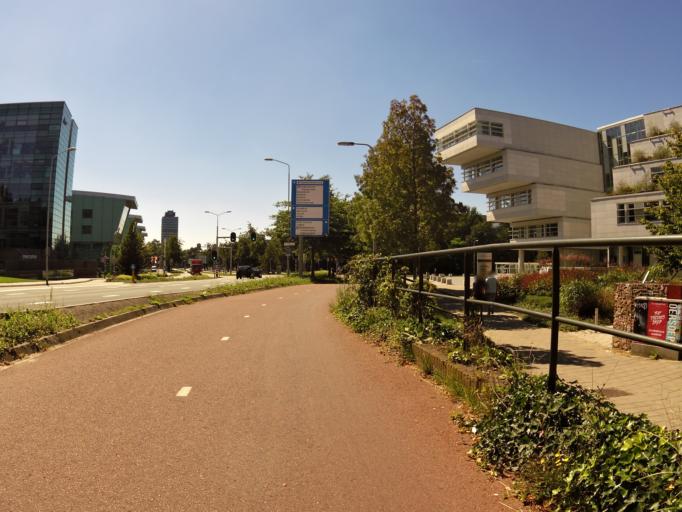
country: NL
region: Gelderland
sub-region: Gemeente Nijmegen
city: Nijmegen
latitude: 51.8260
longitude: 5.8683
